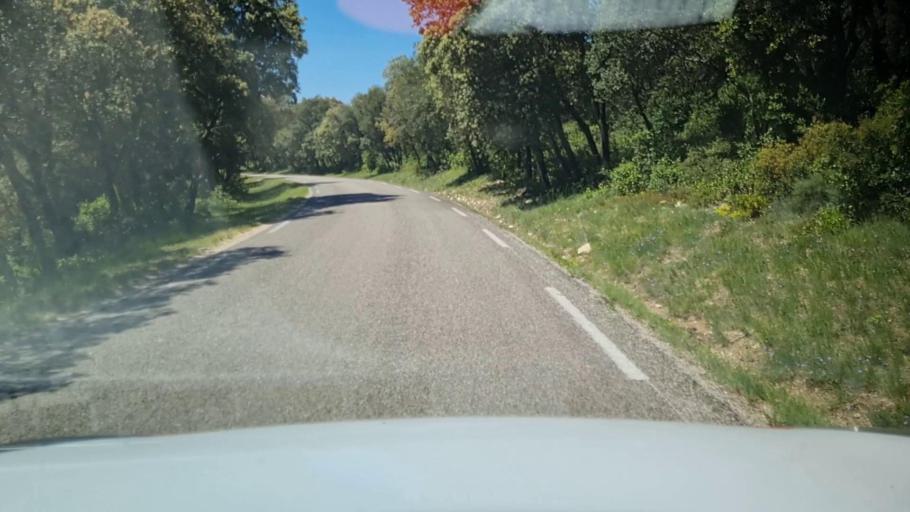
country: FR
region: Languedoc-Roussillon
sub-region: Departement du Gard
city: Clarensac
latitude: 43.8490
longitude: 4.2201
